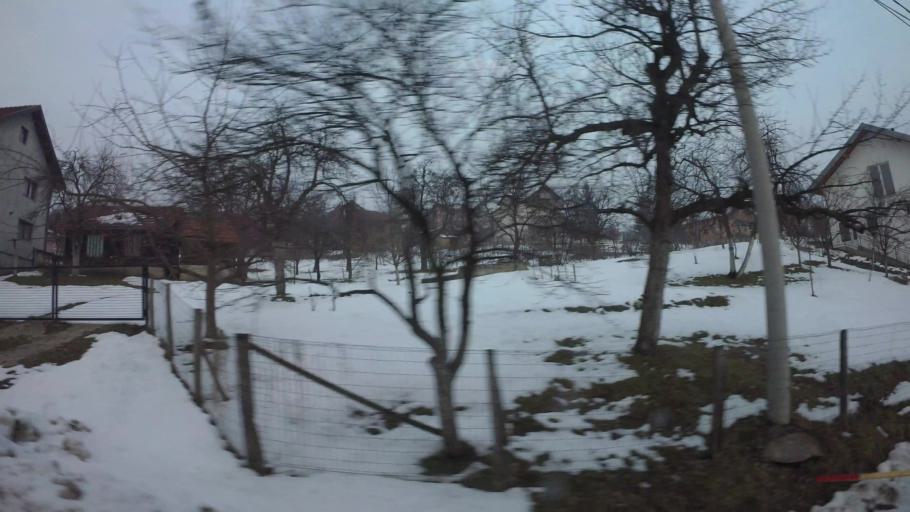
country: BA
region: Federation of Bosnia and Herzegovina
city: Vogosca
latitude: 43.9051
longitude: 18.3509
